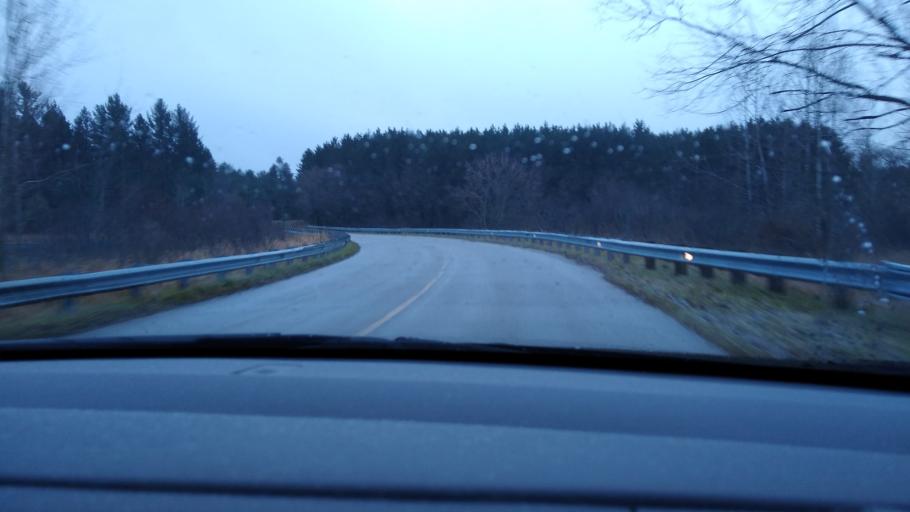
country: US
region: Michigan
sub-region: Wexford County
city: Cadillac
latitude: 44.1852
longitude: -85.3959
